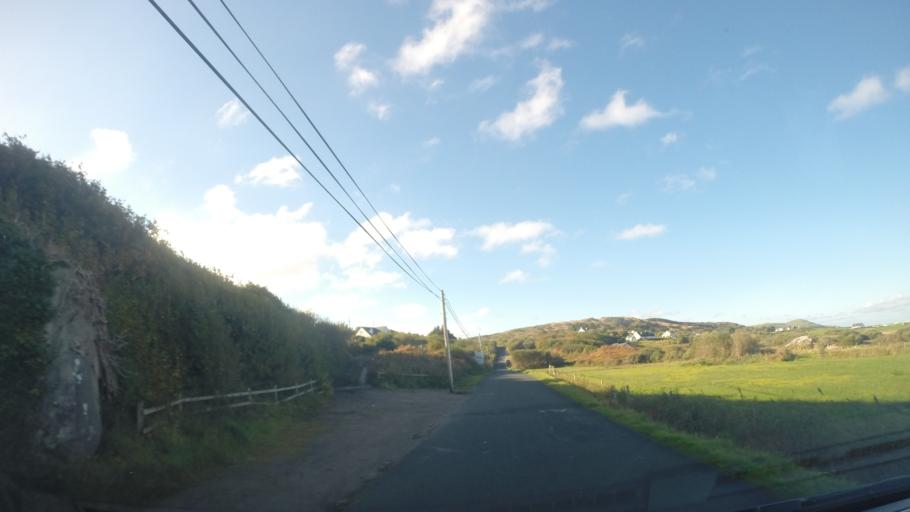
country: IE
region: Ulster
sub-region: County Donegal
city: Dungloe
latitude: 54.8356
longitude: -8.4300
